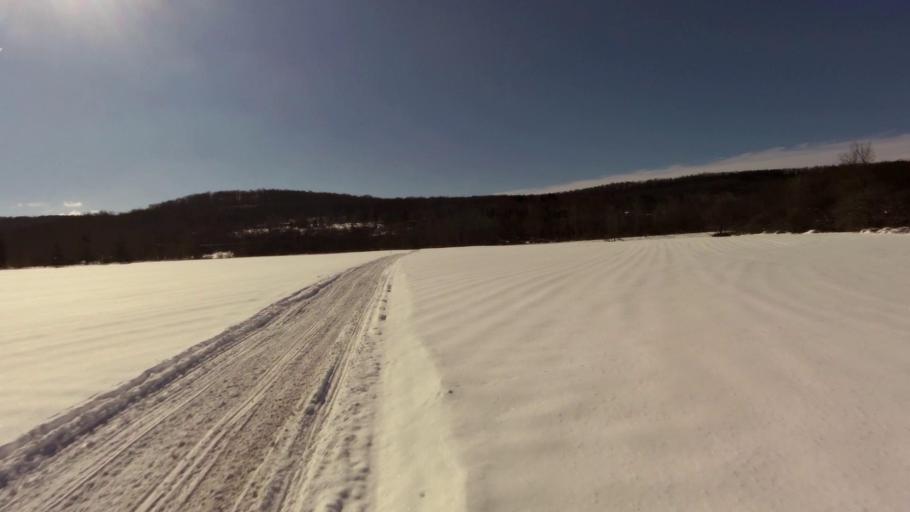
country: US
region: New York
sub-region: Cattaraugus County
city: Franklinville
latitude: 42.3459
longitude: -78.4293
